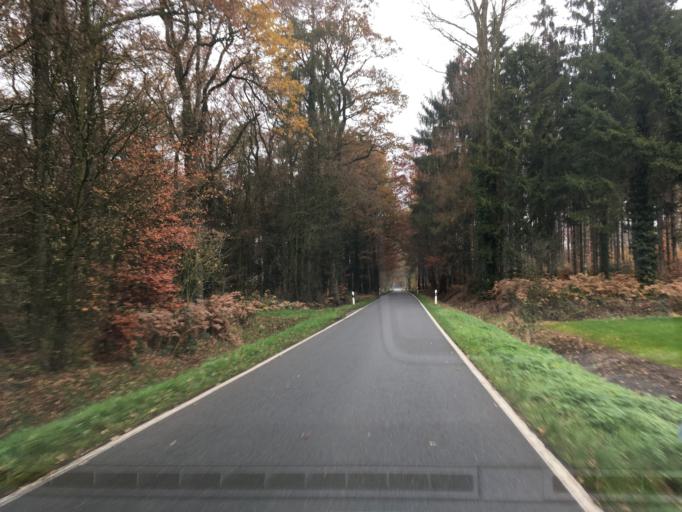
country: DE
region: North Rhine-Westphalia
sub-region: Regierungsbezirk Munster
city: Gescher
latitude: 52.0126
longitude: 6.9968
